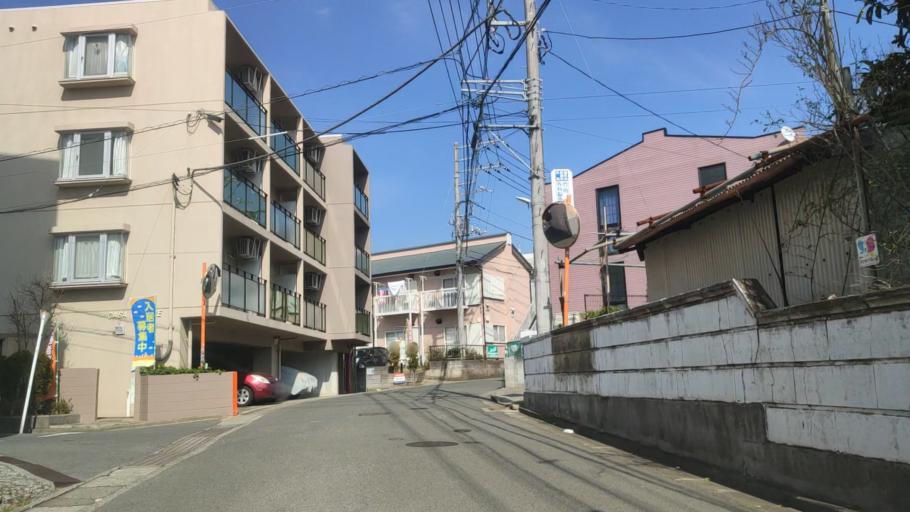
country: JP
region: Kanagawa
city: Isehara
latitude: 35.3835
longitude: 139.2801
